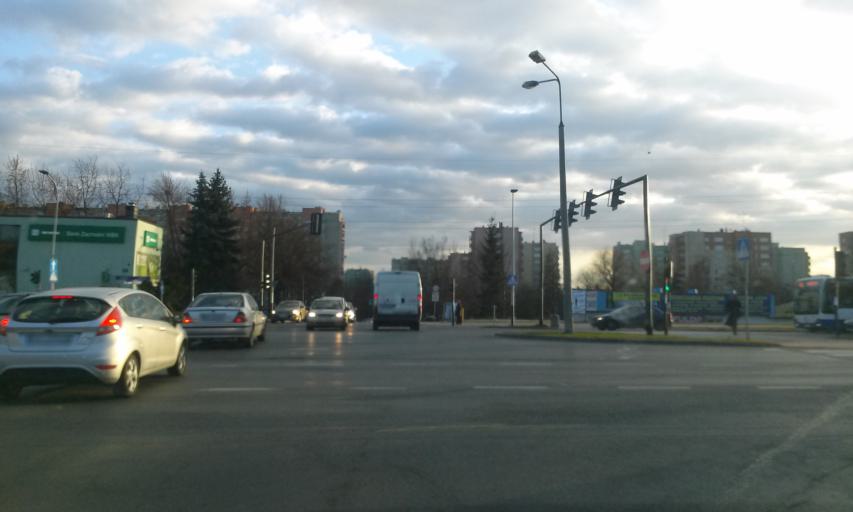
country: PL
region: Lesser Poland Voivodeship
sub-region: Powiat krakowski
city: Michalowice
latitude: 50.0862
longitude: 20.0135
